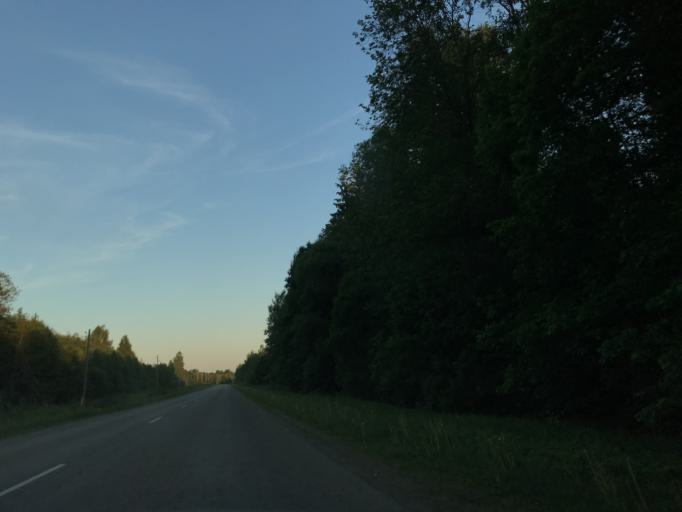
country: LV
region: Jaunjelgava
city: Jaunjelgava
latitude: 56.3563
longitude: 25.0492
